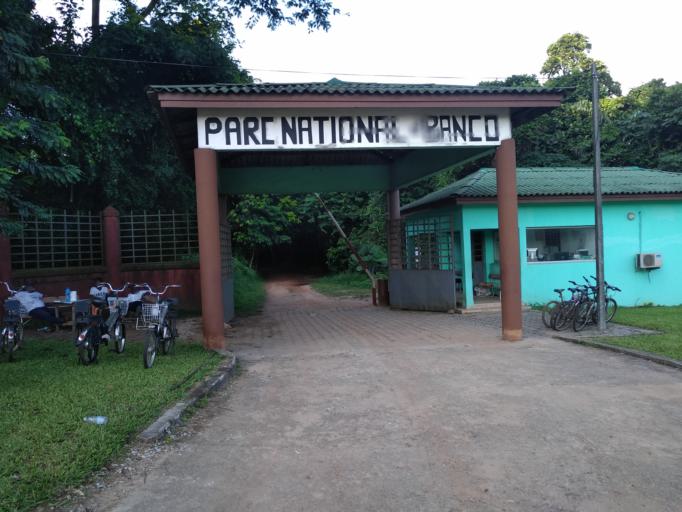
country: CI
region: Lagunes
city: Abidjan
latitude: 5.3604
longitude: -4.0466
